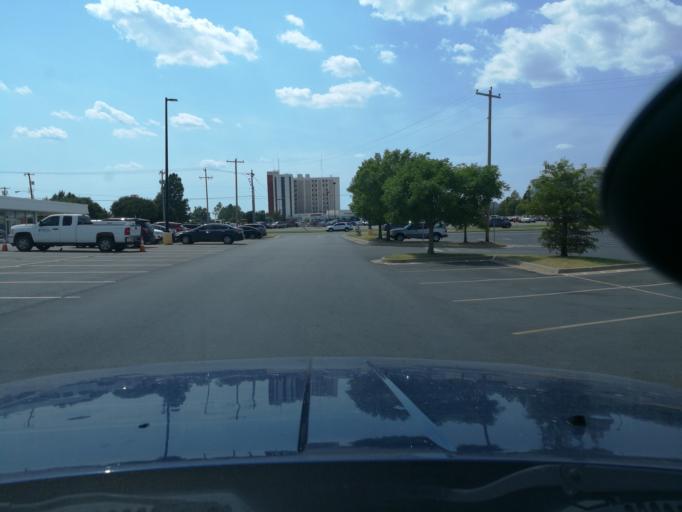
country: US
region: Oklahoma
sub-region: Oklahoma County
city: Oklahoma City
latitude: 35.4215
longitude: -97.5292
